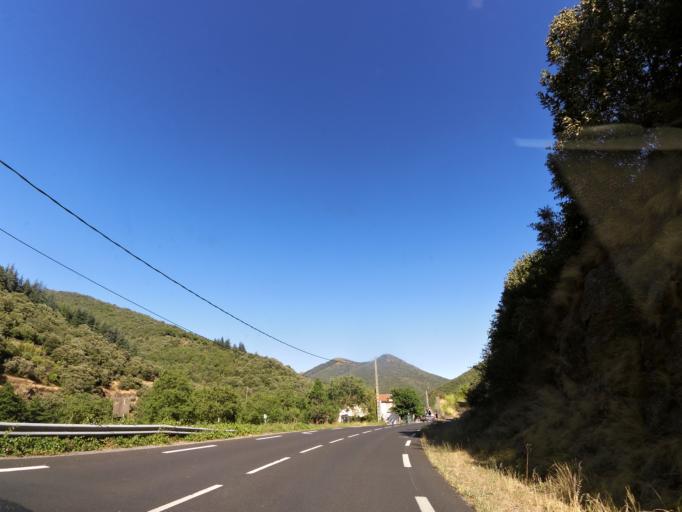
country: FR
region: Languedoc-Roussillon
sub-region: Departement du Gard
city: Valleraugue
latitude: 44.0793
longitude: 3.6501
